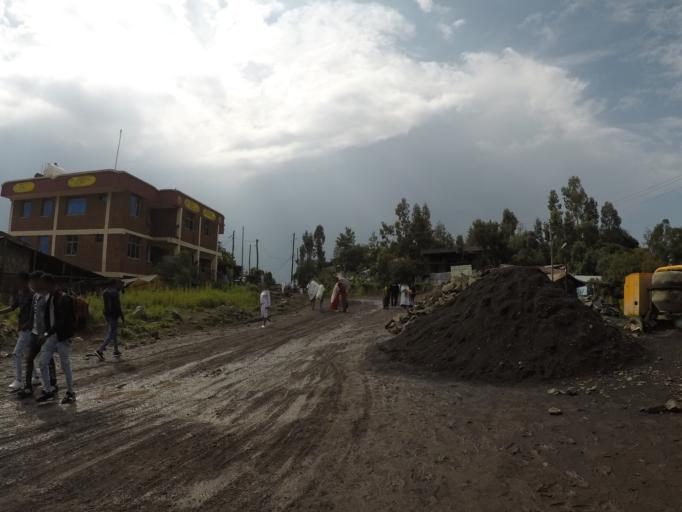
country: ET
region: Amhara
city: Lalibela
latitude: 12.0396
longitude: 39.0524
